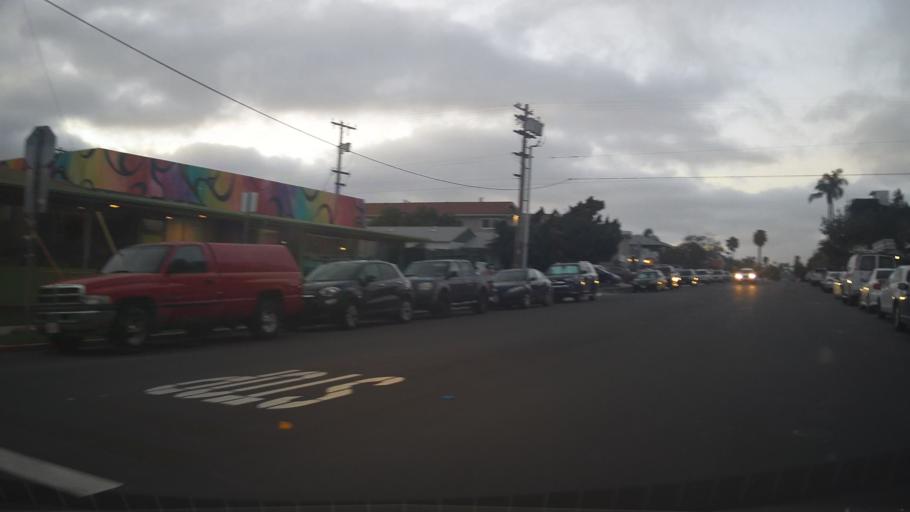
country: US
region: California
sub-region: San Diego County
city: San Diego
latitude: 32.7555
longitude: -117.1412
